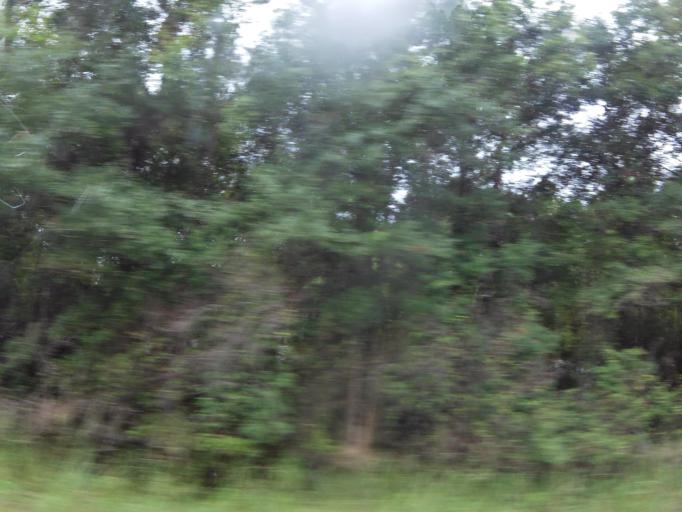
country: US
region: Florida
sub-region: Baker County
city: Macclenny
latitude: 30.5227
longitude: -82.1534
